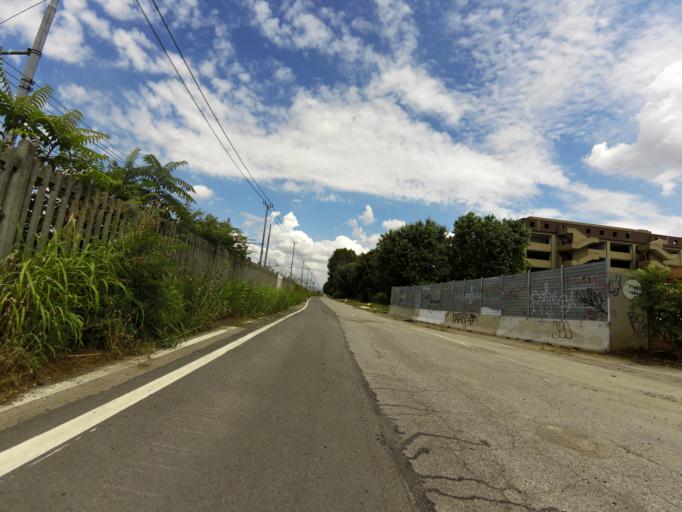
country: IT
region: Lombardy
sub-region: Citta metropolitana di Milano
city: Chiaravalle
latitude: 45.4384
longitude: 9.2378
